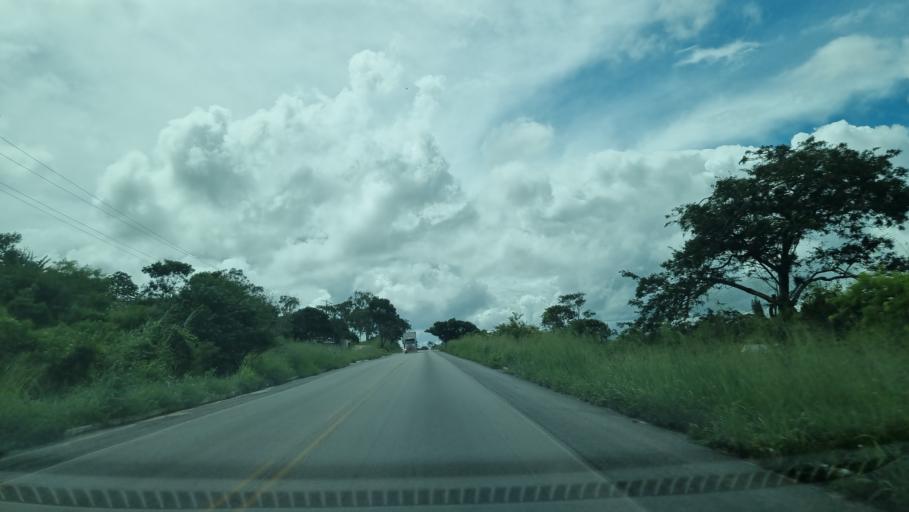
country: BR
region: Pernambuco
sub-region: Caruaru
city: Caruaru
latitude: -8.3488
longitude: -35.9847
